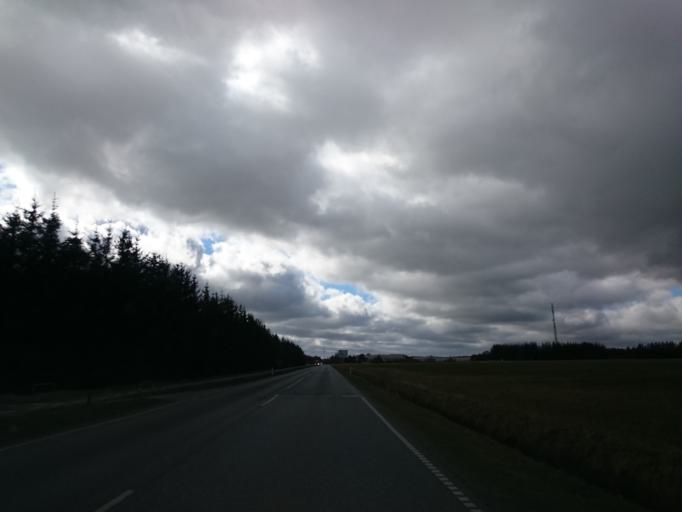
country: DK
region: North Denmark
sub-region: Frederikshavn Kommune
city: Strandby
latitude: 57.6082
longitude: 10.4267
